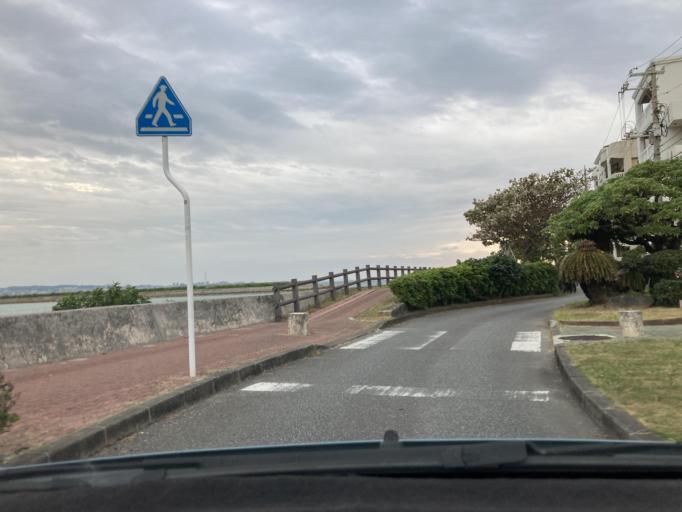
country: JP
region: Okinawa
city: Chatan
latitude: 26.3214
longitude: 127.7514
